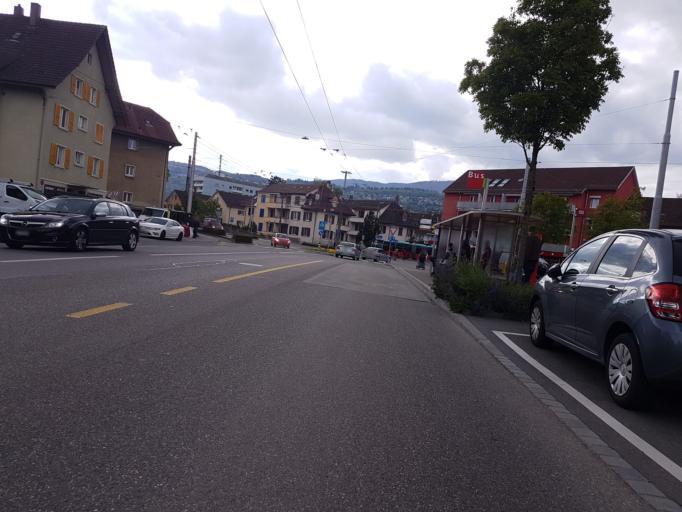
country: CH
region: Bern
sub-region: Biel/Bienne District
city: Brugg
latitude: 47.1435
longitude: 7.2759
